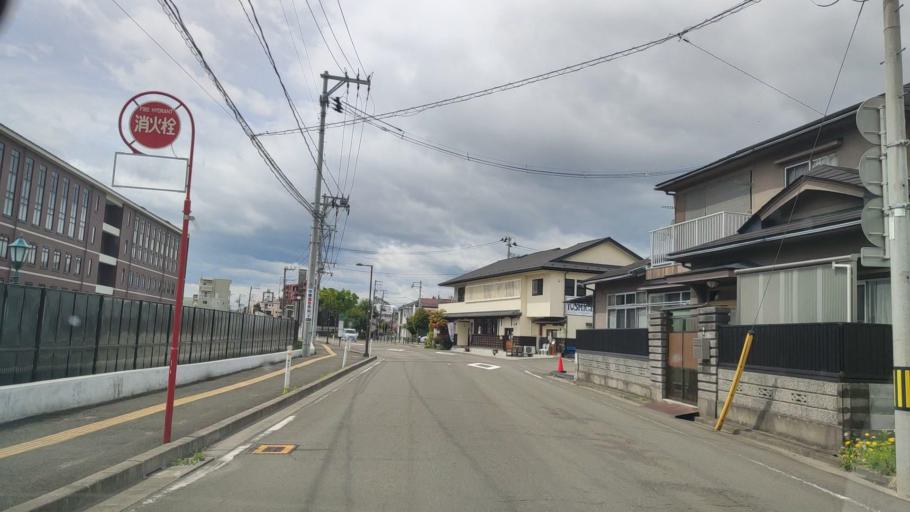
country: JP
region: Miyagi
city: Sendai-shi
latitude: 38.2617
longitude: 140.9038
